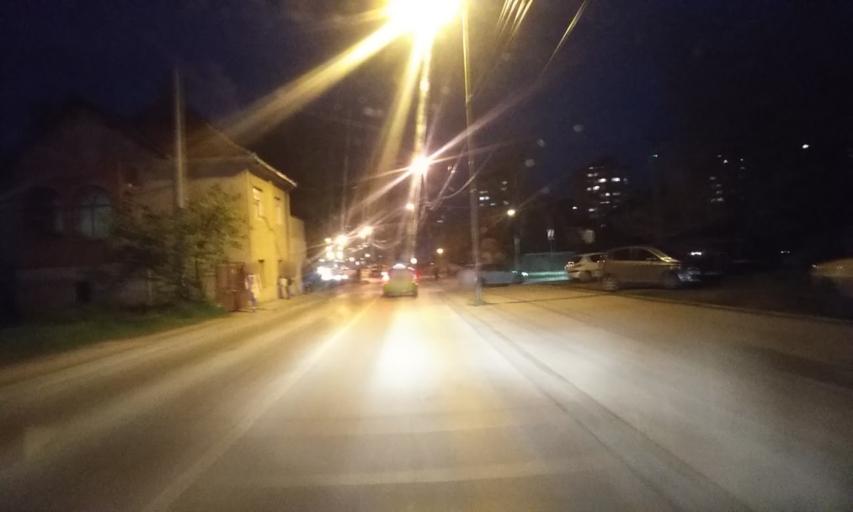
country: RS
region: Central Serbia
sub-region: Nisavski Okrug
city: Nis
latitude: 43.3283
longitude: 21.9089
